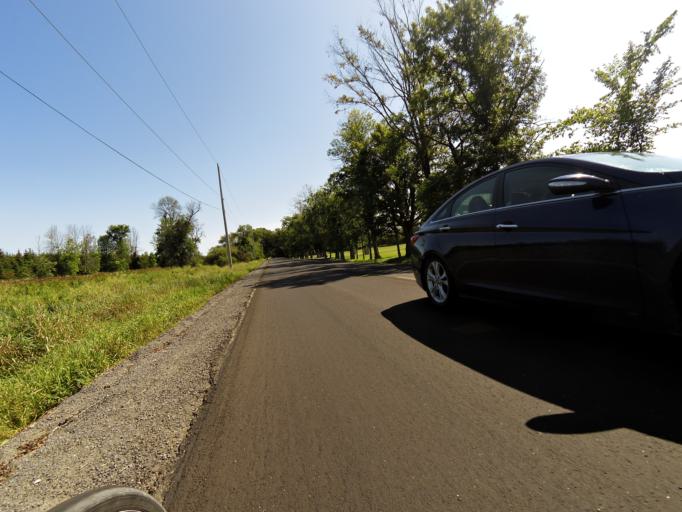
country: CA
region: Ontario
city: Bells Corners
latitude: 45.3752
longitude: -75.9346
